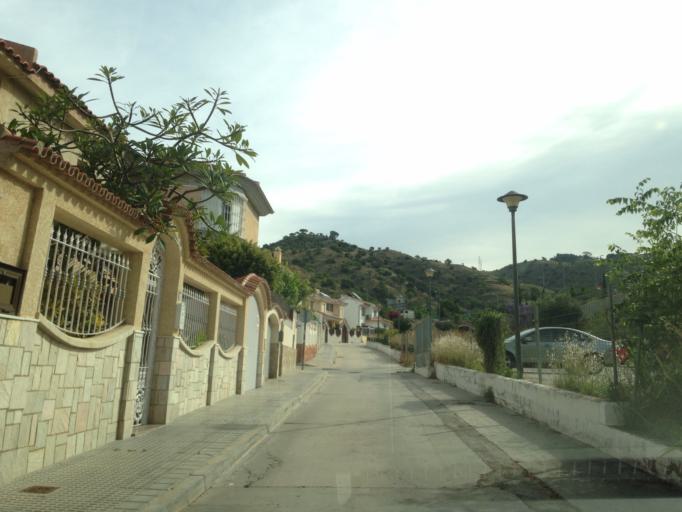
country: ES
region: Andalusia
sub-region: Provincia de Malaga
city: Malaga
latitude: 36.7552
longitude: -4.4226
